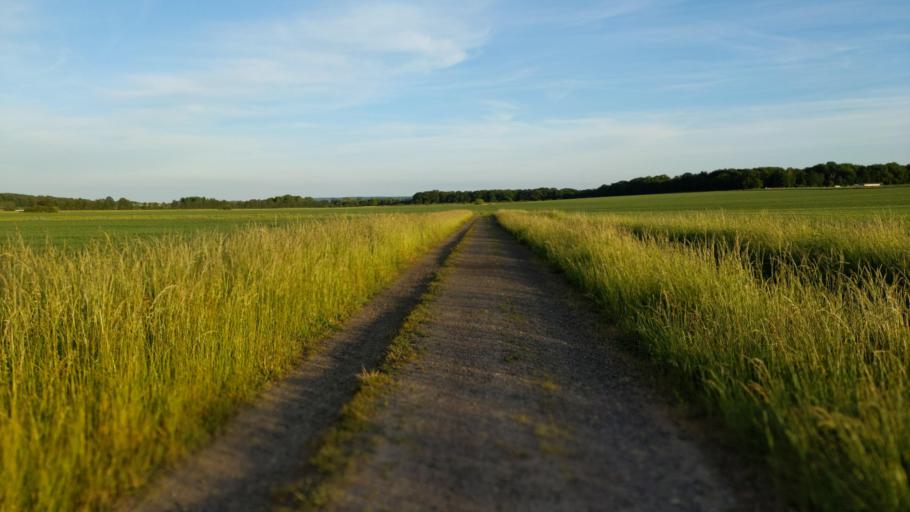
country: DE
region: Lower Saxony
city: Sickte
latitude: 52.2334
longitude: 10.5869
